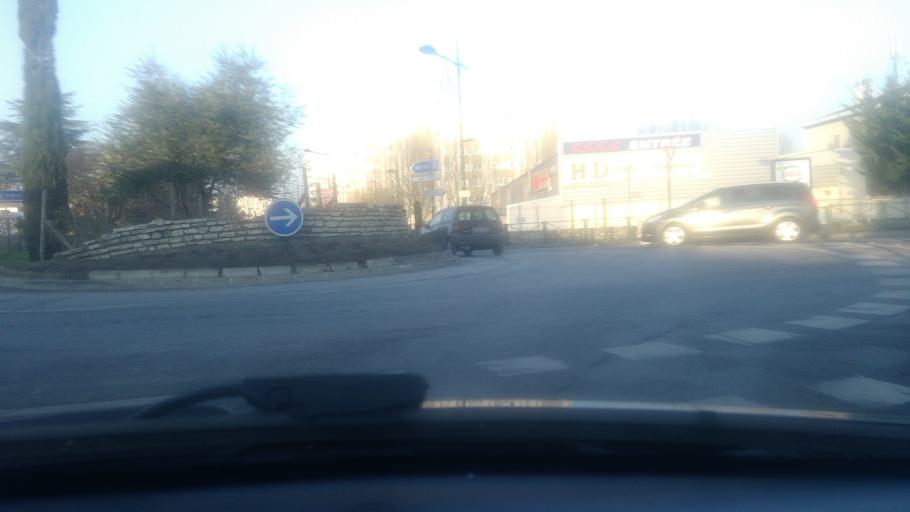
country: FR
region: Ile-de-France
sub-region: Departement du Val-d'Oise
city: Franconville
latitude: 48.9792
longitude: 2.2373
